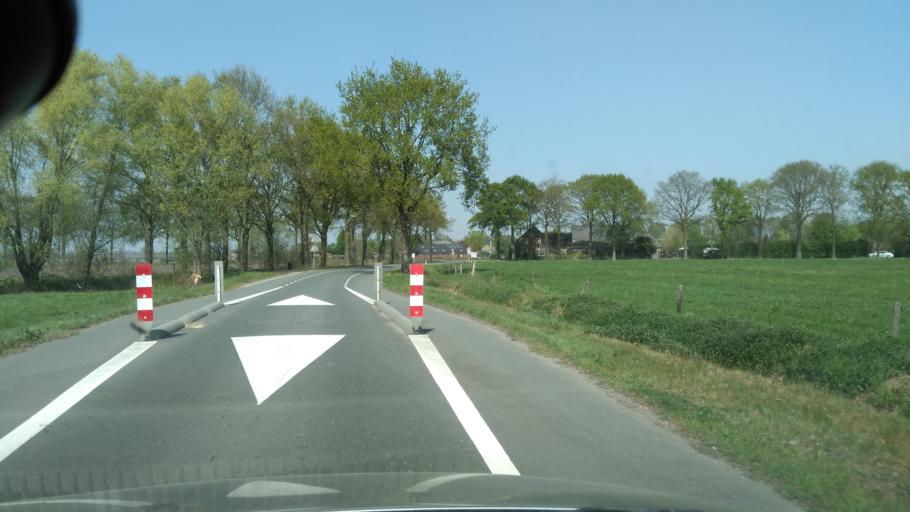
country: NL
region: North Brabant
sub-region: Gemeente Baarle-Nassau
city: Baarle-Nassau
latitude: 51.4858
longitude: 4.8611
